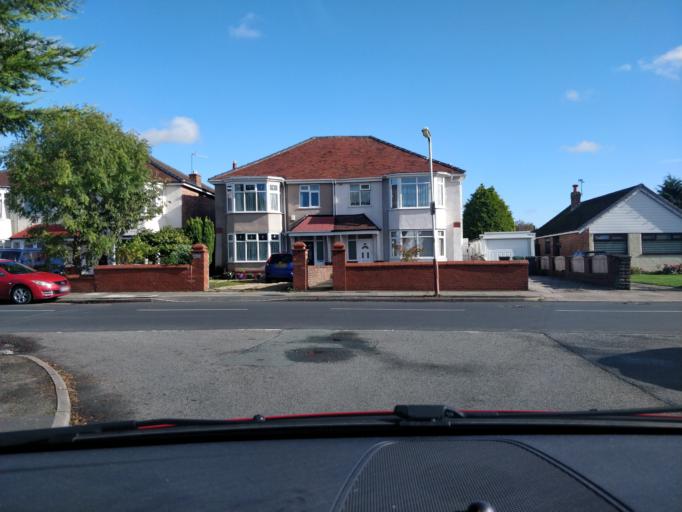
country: GB
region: England
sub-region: Sefton
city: Southport
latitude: 53.6347
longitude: -2.9887
